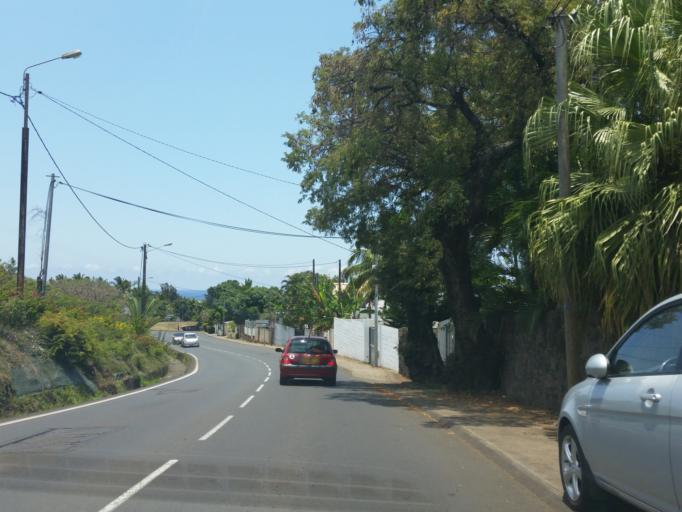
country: RE
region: Reunion
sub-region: Reunion
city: Sainte-Marie
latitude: -20.9067
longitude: 55.5042
